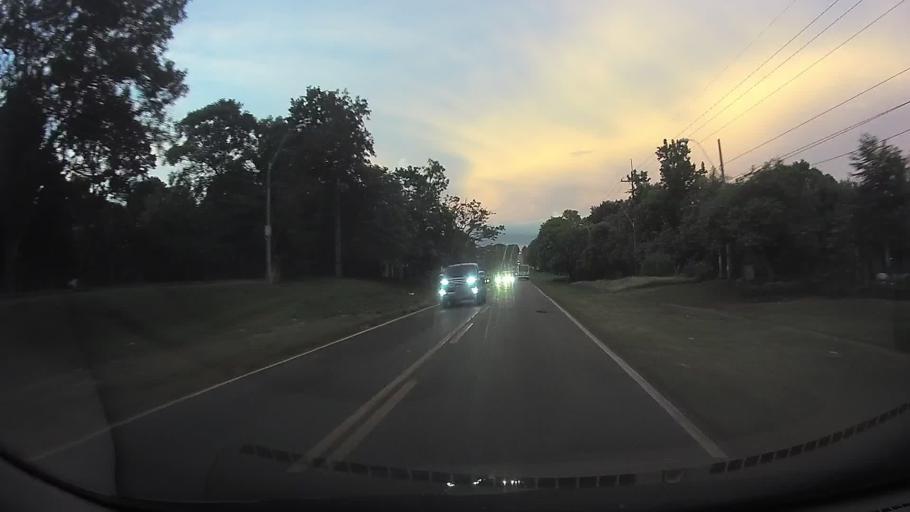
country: PY
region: Central
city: Ita
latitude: -25.4836
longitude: -57.3612
